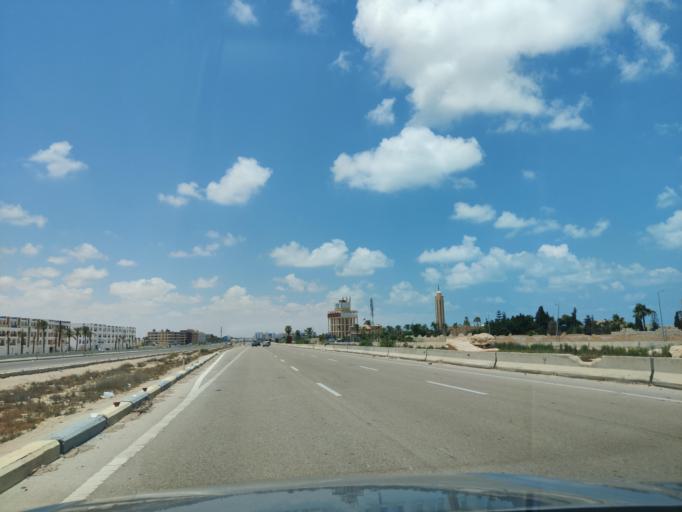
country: EG
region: Muhafazat Matruh
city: Al `Alamayn
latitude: 30.8162
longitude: 29.0344
